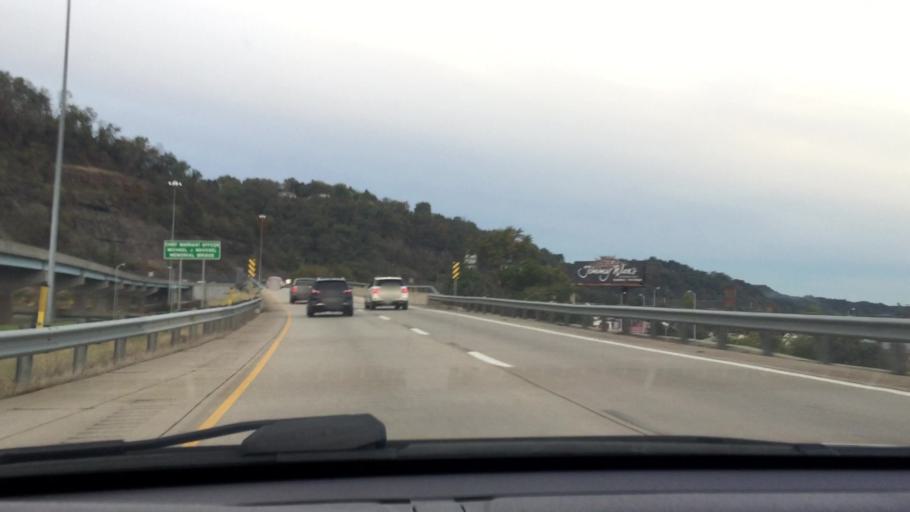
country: US
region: Pennsylvania
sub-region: Allegheny County
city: Etna
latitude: 40.4948
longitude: -79.9412
